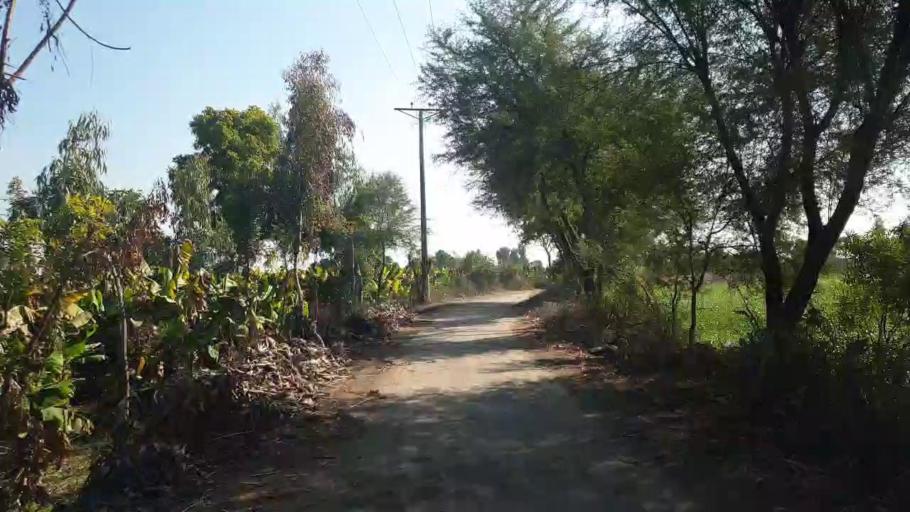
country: PK
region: Sindh
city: Shahdadpur
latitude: 25.9144
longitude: 68.5643
